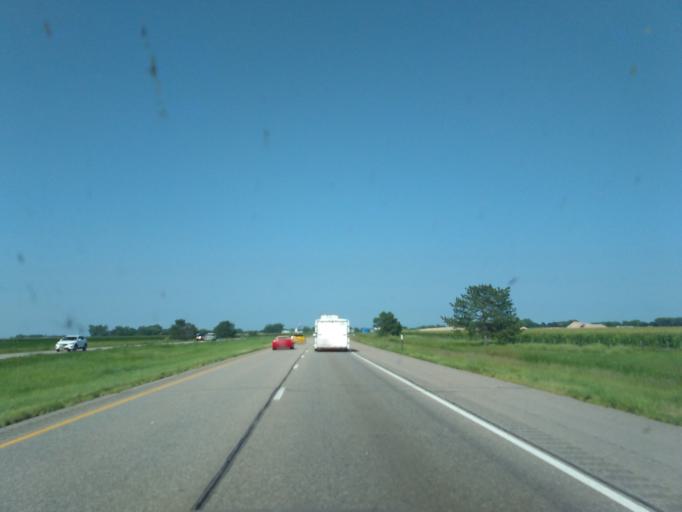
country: US
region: Nebraska
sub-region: Hall County
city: Wood River
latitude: 40.7931
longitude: -98.5109
